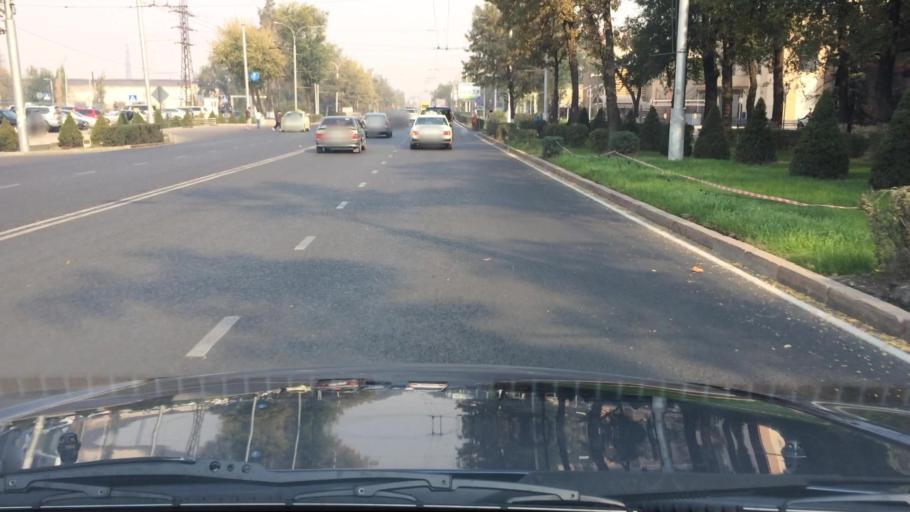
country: KG
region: Chuy
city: Bishkek
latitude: 42.8548
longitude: 74.5867
